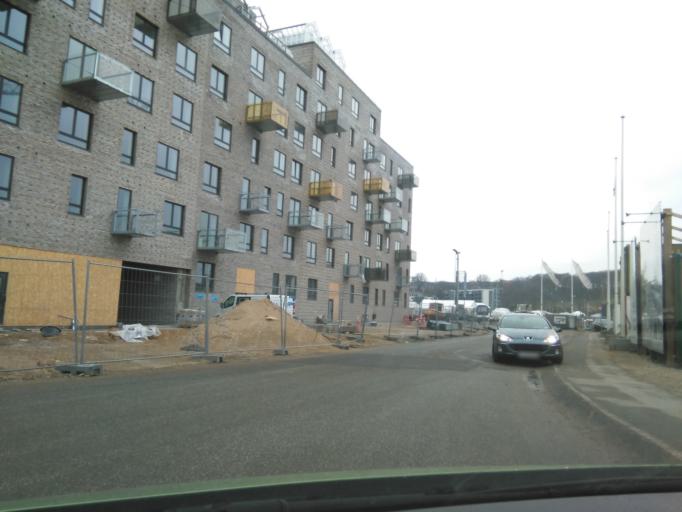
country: DK
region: Central Jutland
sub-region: Arhus Kommune
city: Arhus
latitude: 56.1661
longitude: 10.2266
